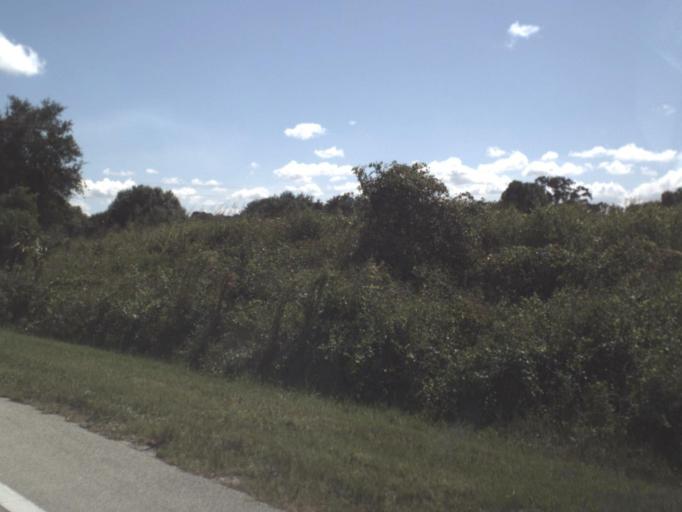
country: US
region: Florida
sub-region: Hendry County
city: Port LaBelle
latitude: 26.8129
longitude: -81.3221
